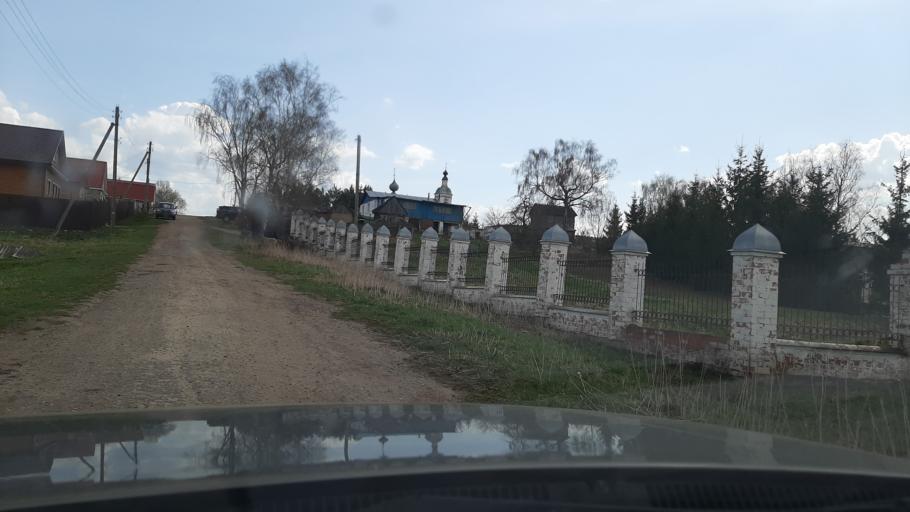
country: RU
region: Ivanovo
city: Privolzhsk
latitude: 57.3344
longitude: 41.2327
